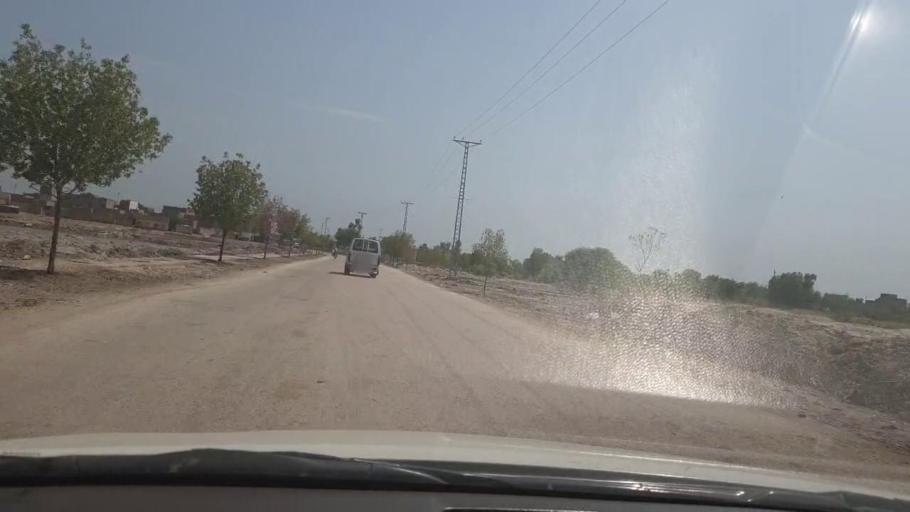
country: PK
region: Sindh
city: Garhi Yasin
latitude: 27.9074
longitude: 68.5064
